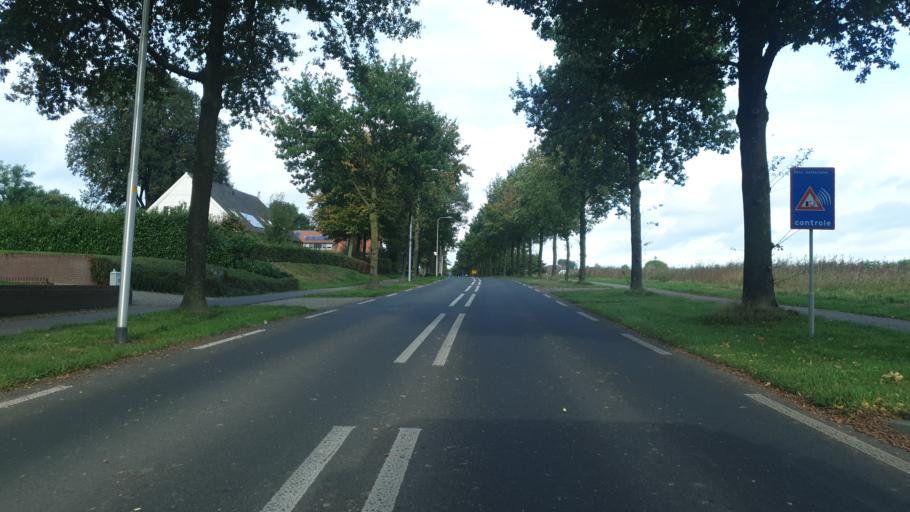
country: NL
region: Gelderland
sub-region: Gemeente Groesbeek
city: Bredeweg
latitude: 51.7632
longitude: 5.9399
